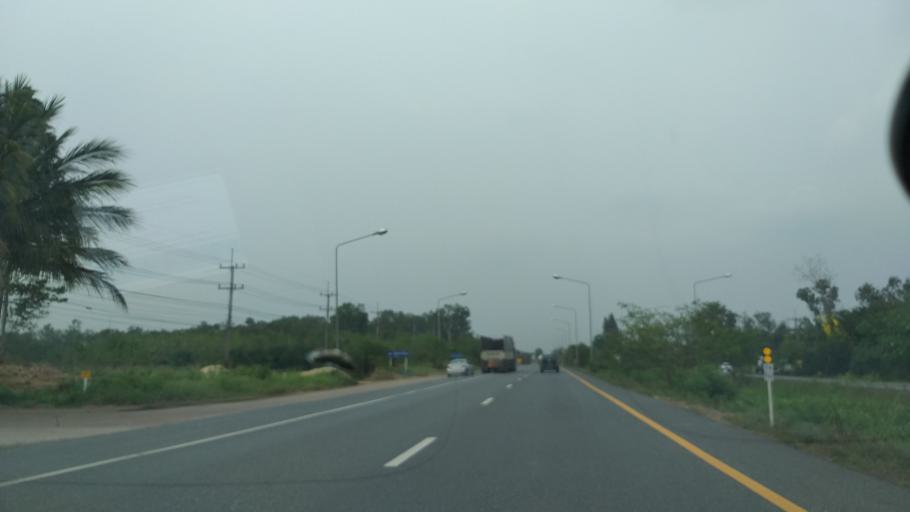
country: TH
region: Chon Buri
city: Ban Bueng
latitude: 13.2782
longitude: 101.2542
